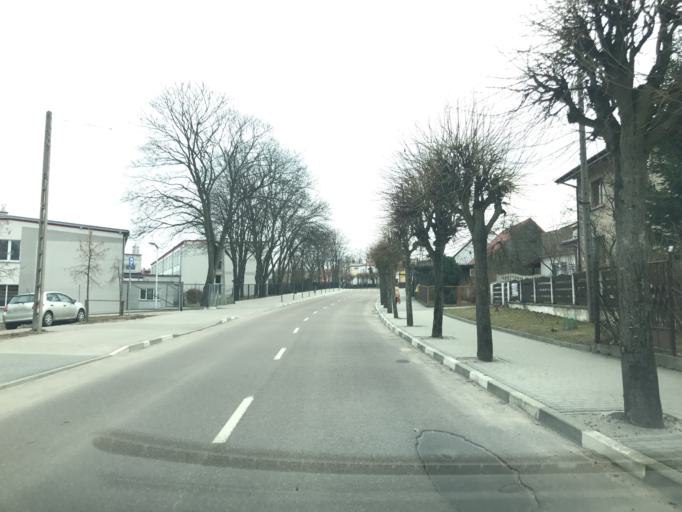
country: PL
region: Warmian-Masurian Voivodeship
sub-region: Powiat dzialdowski
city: Lidzbark
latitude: 53.2615
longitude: 19.8188
